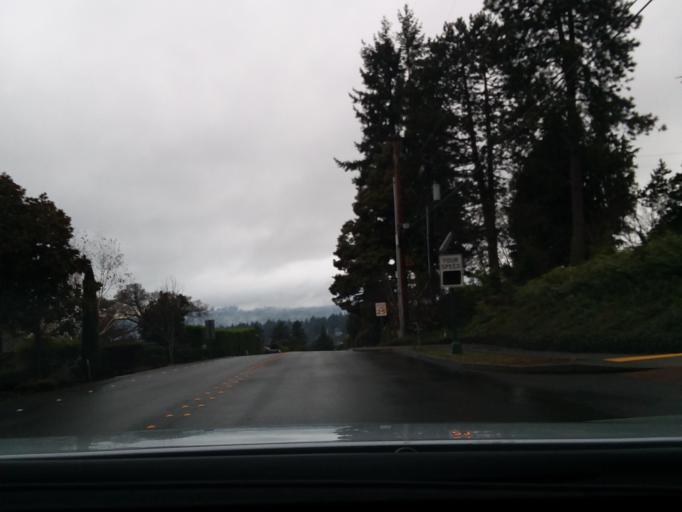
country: US
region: Washington
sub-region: King County
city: Clyde Hill
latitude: 47.6230
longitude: -122.2134
